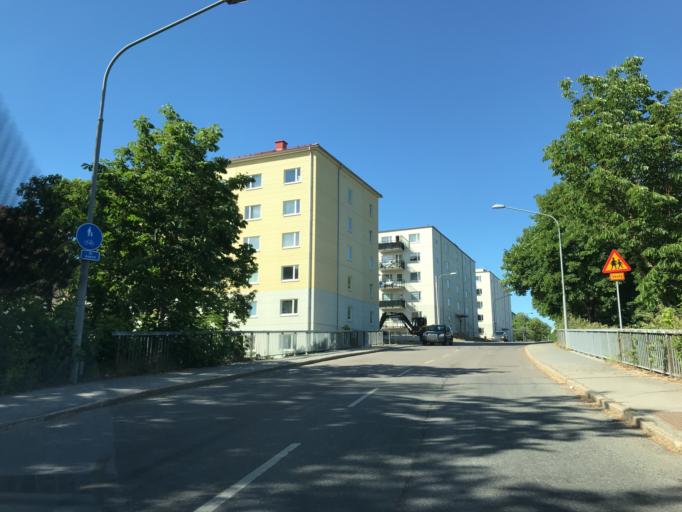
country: SE
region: Stockholm
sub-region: Huddinge Kommun
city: Segeltorp
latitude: 59.2893
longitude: 17.9389
